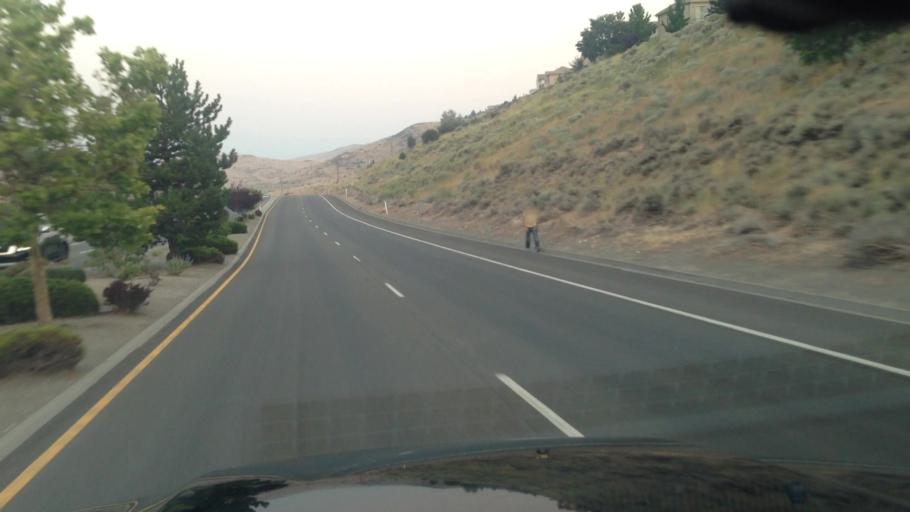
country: US
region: Nevada
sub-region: Washoe County
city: Reno
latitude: 39.4841
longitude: -119.8520
